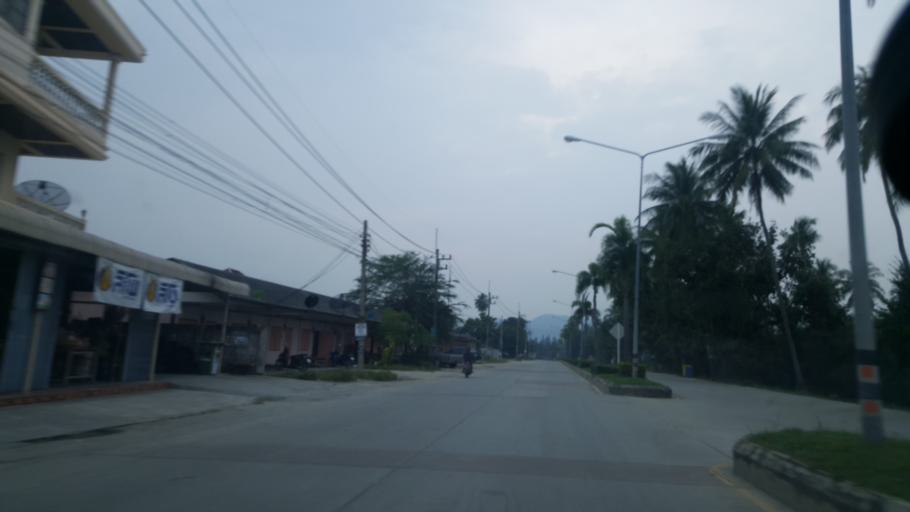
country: TH
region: Chon Buri
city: Si Racha
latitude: 13.2368
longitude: 101.0085
